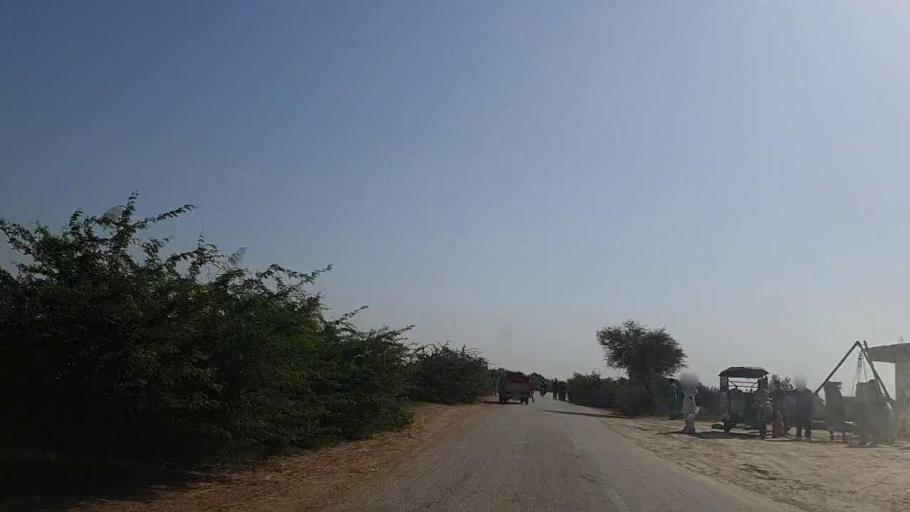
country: PK
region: Sindh
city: Mirpur Batoro
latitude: 24.6089
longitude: 68.2961
